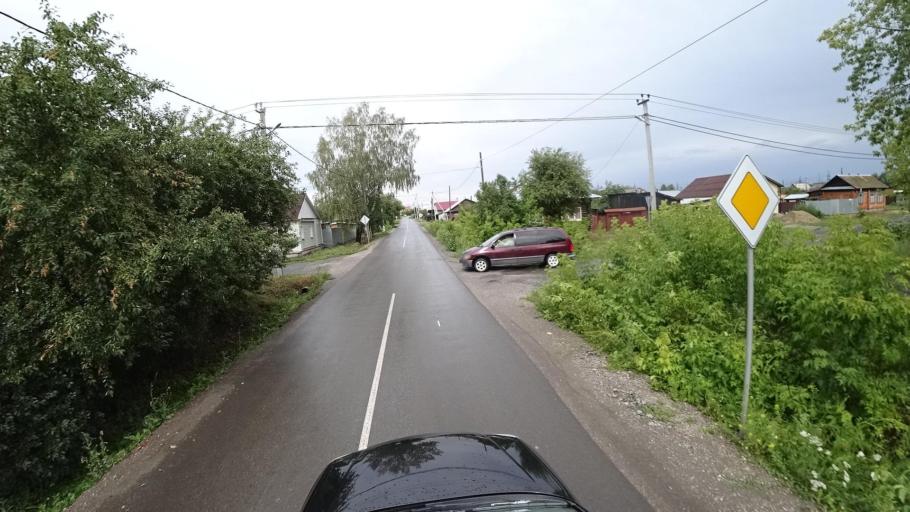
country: RU
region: Sverdlovsk
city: Kamyshlov
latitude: 56.8504
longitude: 62.7357
